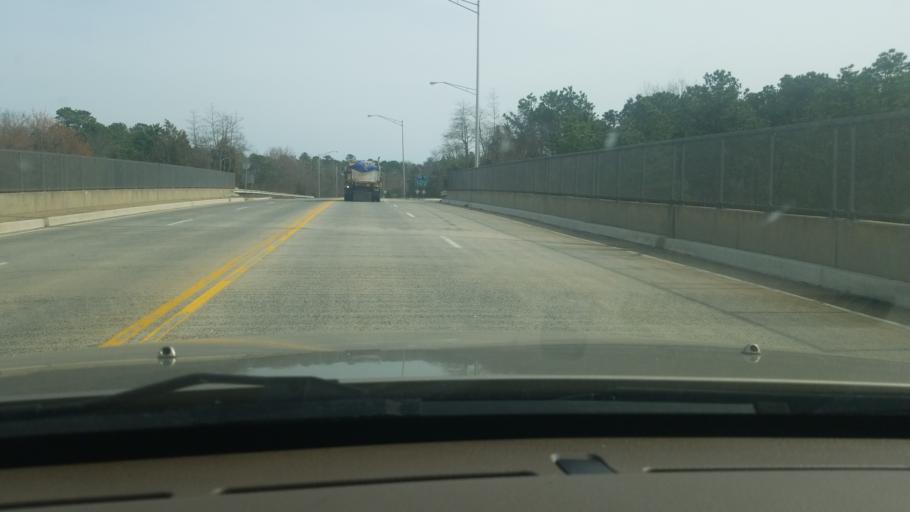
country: US
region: New Jersey
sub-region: Ocean County
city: Vista Center
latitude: 40.1548
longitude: -74.3463
